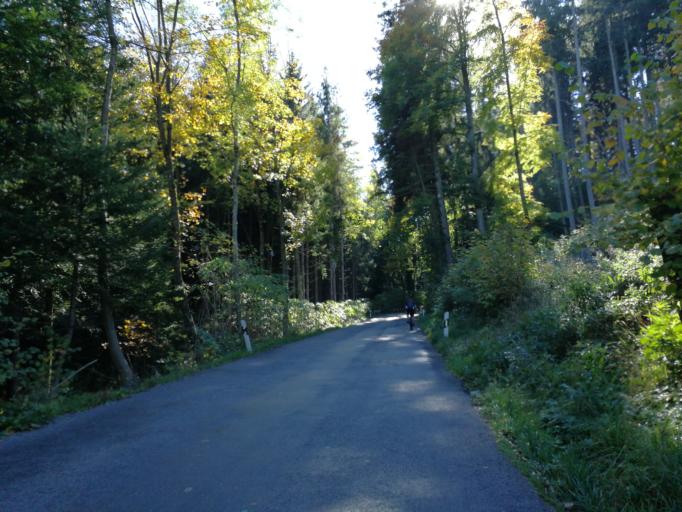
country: CH
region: Zurich
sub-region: Bezirk Uster
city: Hinteregg
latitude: 47.2973
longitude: 8.6798
